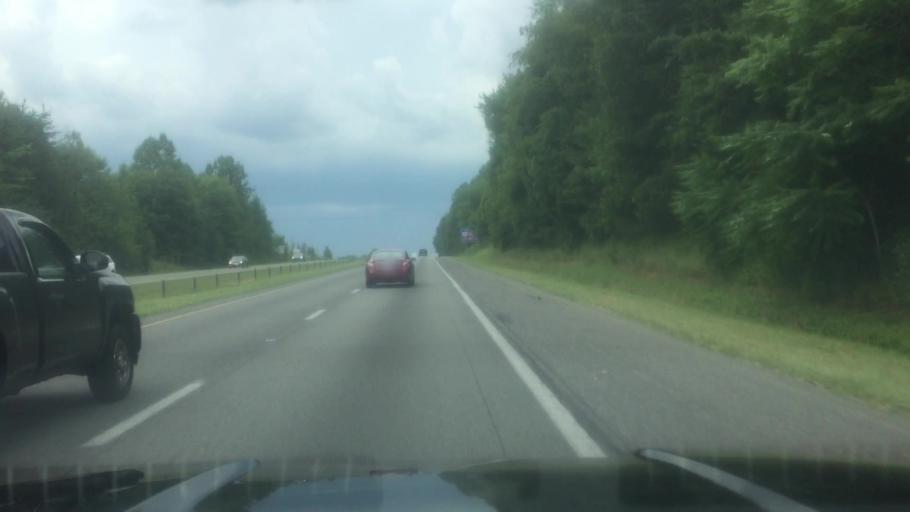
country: US
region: North Carolina
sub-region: Surry County
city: Pilot Mountain
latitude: 36.3662
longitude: -80.4819
